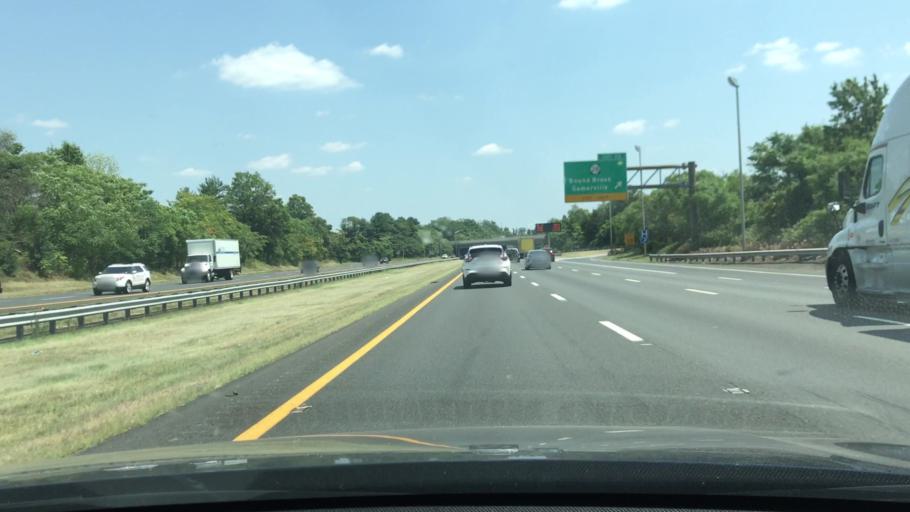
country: US
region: New Jersey
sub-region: Somerset County
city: Finderne
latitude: 40.5707
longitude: -74.5614
